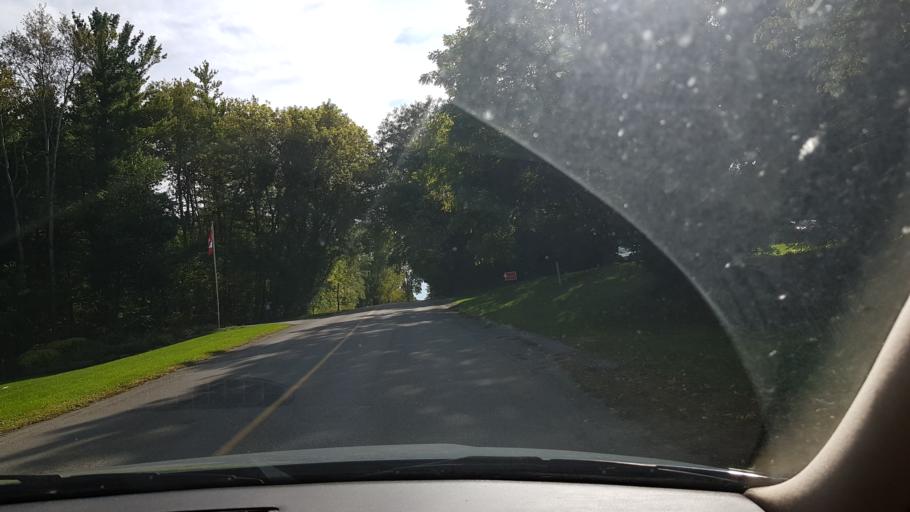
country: CA
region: Ontario
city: Delaware
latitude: 42.9158
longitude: -81.4689
